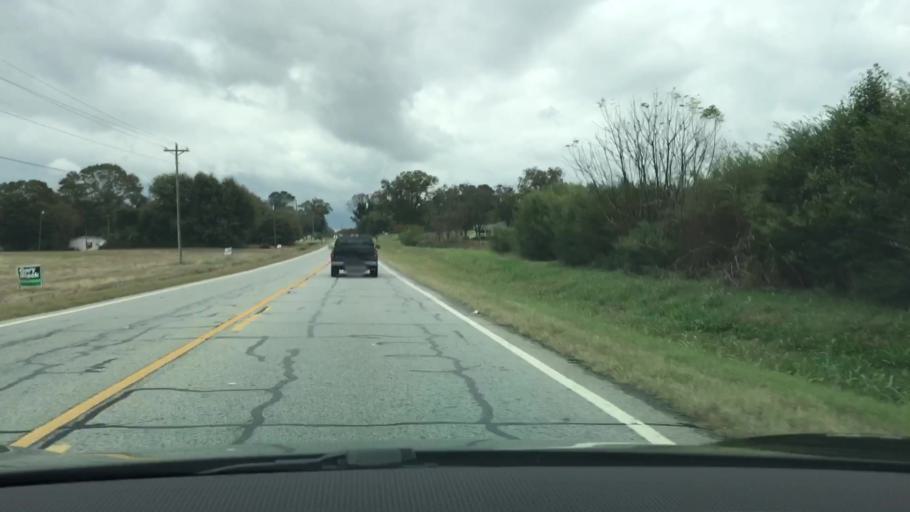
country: US
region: Georgia
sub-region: Oconee County
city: Watkinsville
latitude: 33.8400
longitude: -83.3856
